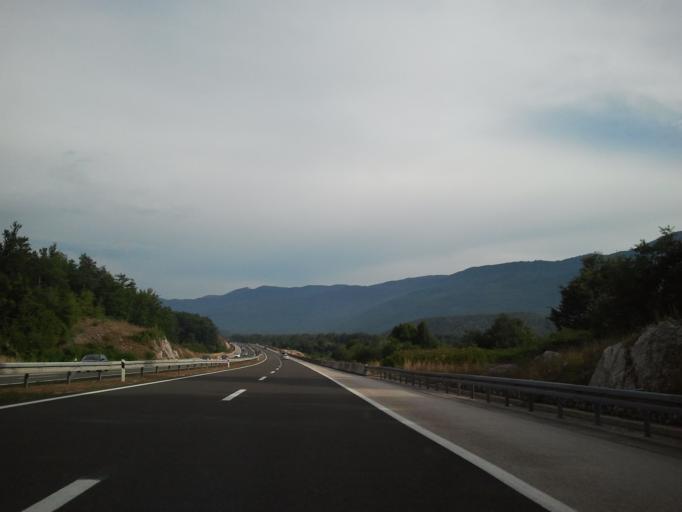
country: HR
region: Zadarska
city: Obrovac
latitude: 44.3551
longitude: 15.6411
